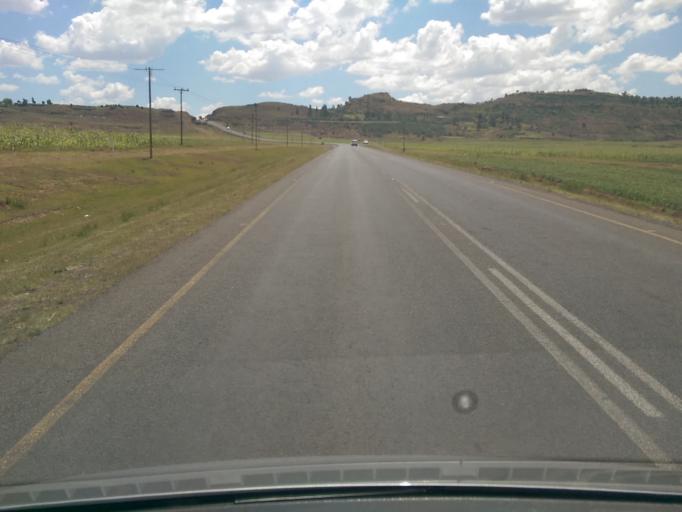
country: LS
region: Maseru
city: Maseru
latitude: -29.4182
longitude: 27.6412
